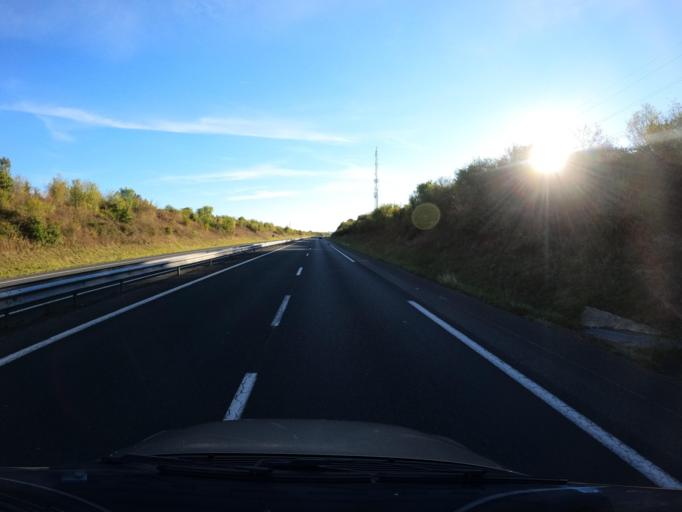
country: FR
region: Pays de la Loire
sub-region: Departement de Maine-et-Loire
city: Mazieres-en-Mauges
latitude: 47.0491
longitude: -0.8372
